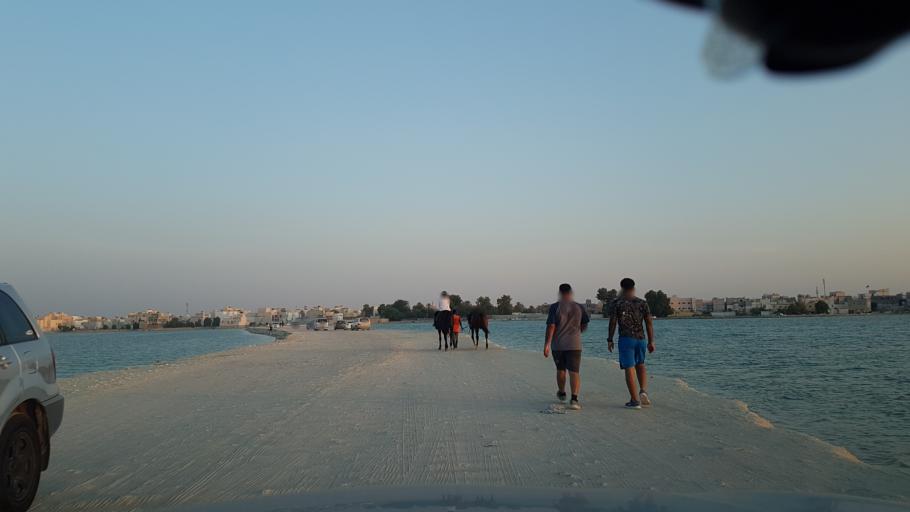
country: BH
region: Manama
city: Jidd Hafs
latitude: 26.2404
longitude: 50.5031
